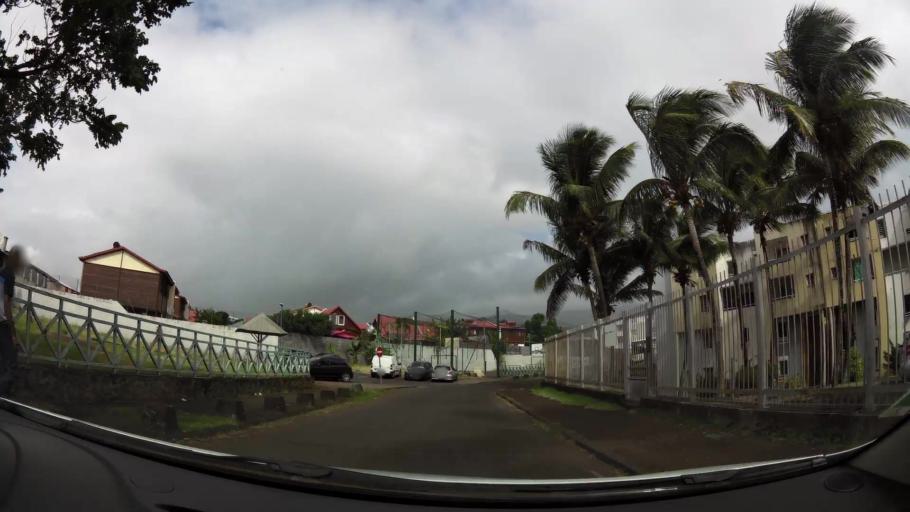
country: RE
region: Reunion
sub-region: Reunion
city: Sainte-Marie
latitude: -20.8996
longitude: 55.5557
